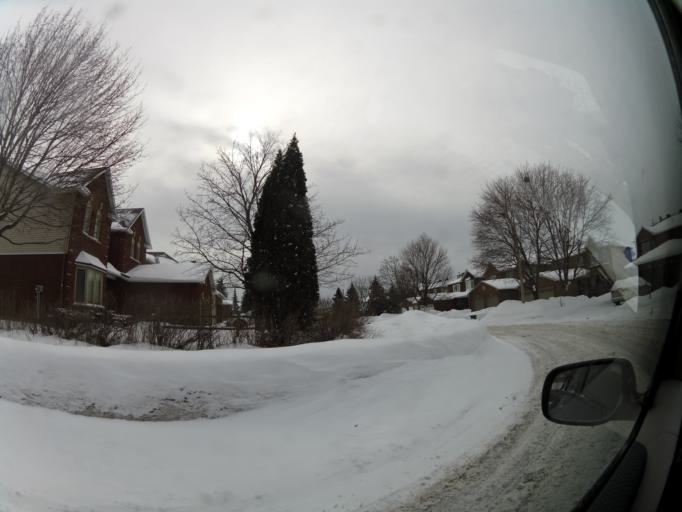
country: CA
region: Ontario
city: Ottawa
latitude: 45.3763
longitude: -75.6053
